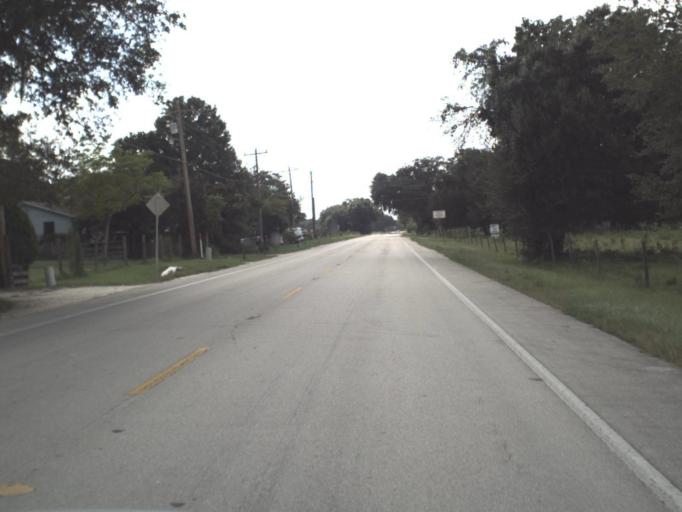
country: US
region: Florida
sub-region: Hardee County
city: Zolfo Springs
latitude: 27.5029
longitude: -81.7749
